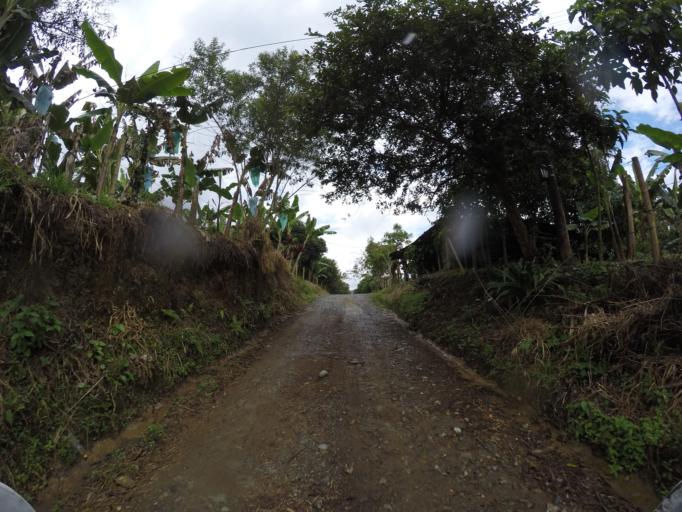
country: CO
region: Valle del Cauca
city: Ulloa
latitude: 4.6835
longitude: -75.7087
